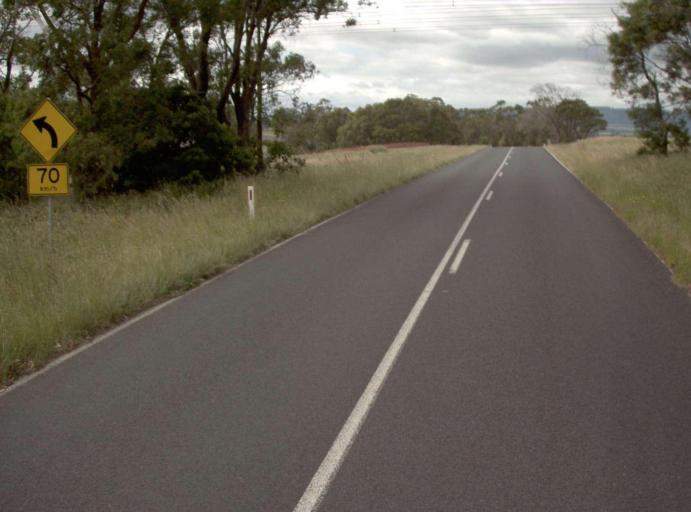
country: AU
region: Victoria
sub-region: Latrobe
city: Moe
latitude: -38.1023
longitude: 146.2379
